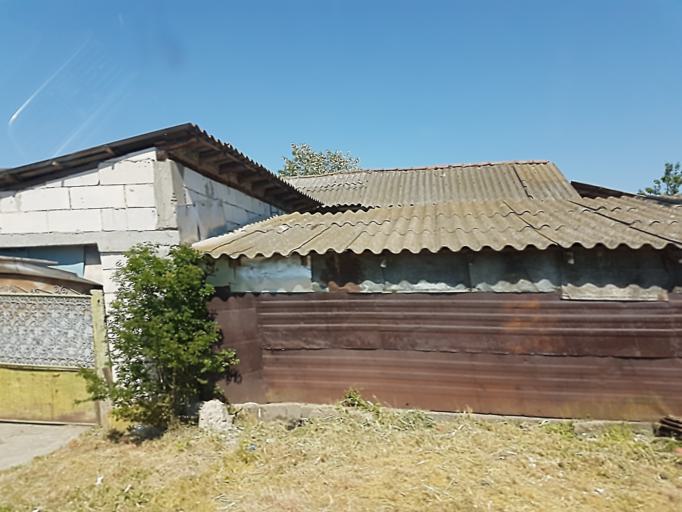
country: RO
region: Giurgiu
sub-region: Comuna Herasti
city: Herasti
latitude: 44.2148
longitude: 26.3591
